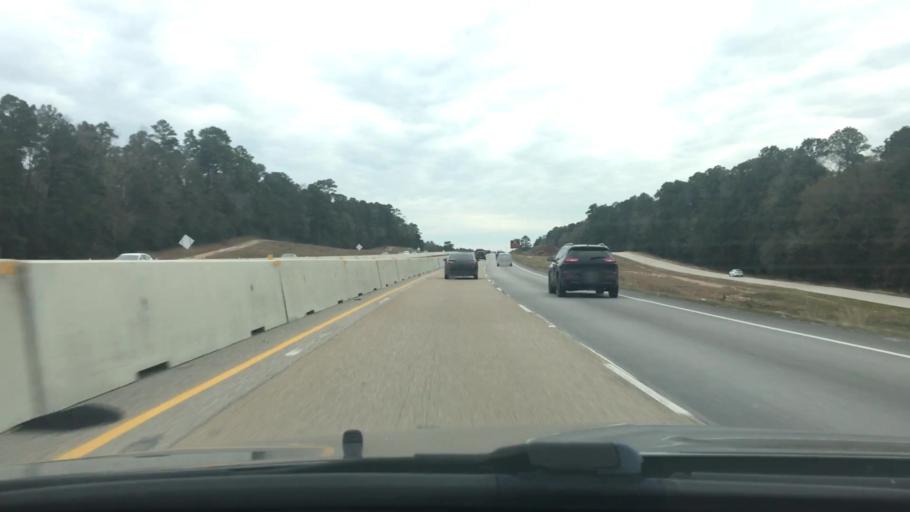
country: US
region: Texas
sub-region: Walker County
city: Huntsville
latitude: 30.6576
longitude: -95.5106
